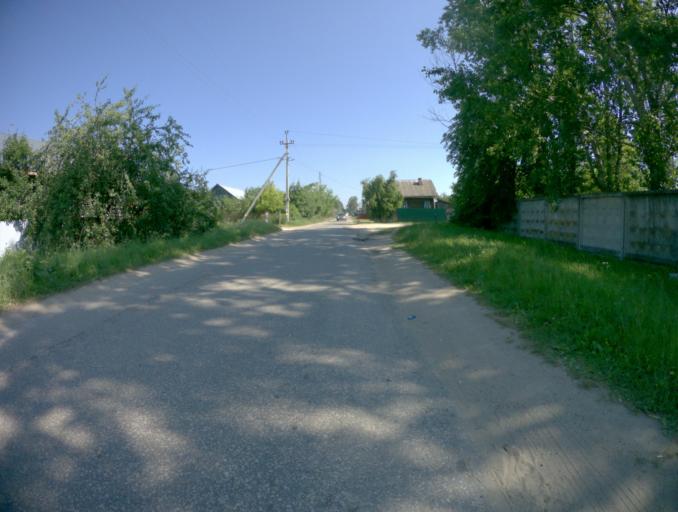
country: RU
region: Vladimir
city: Vyazniki
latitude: 56.2336
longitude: 42.1950
